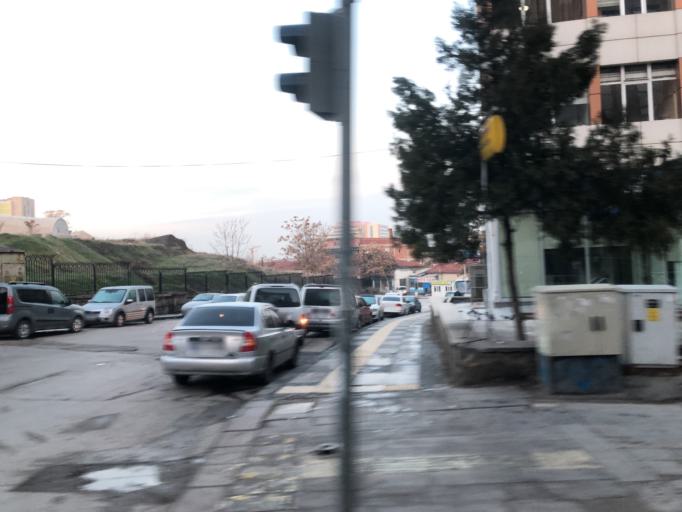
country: TR
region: Ankara
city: Ankara
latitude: 39.9476
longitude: 32.8556
